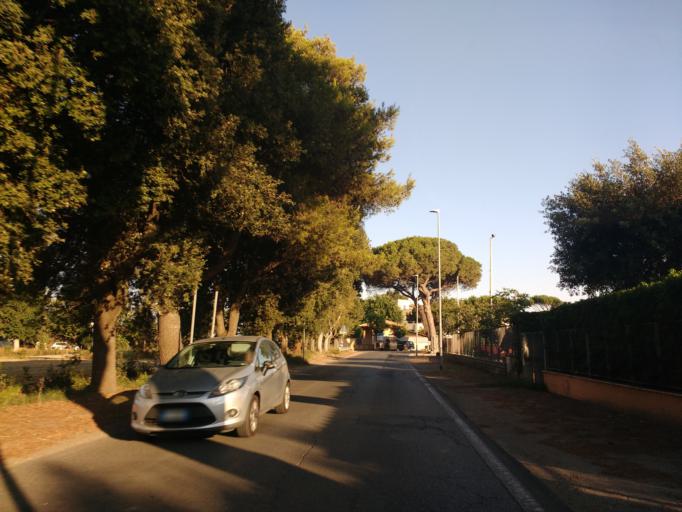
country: IT
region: Latium
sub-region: Citta metropolitana di Roma Capitale
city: Fregene
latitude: 41.8549
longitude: 12.2180
